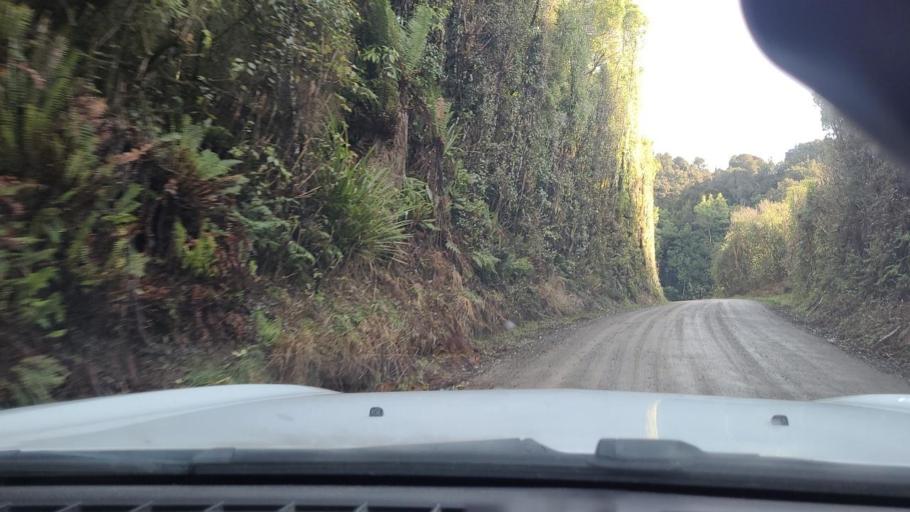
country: NZ
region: Otago
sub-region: Clutha District
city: Papatowai
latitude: -46.4950
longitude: 169.1593
